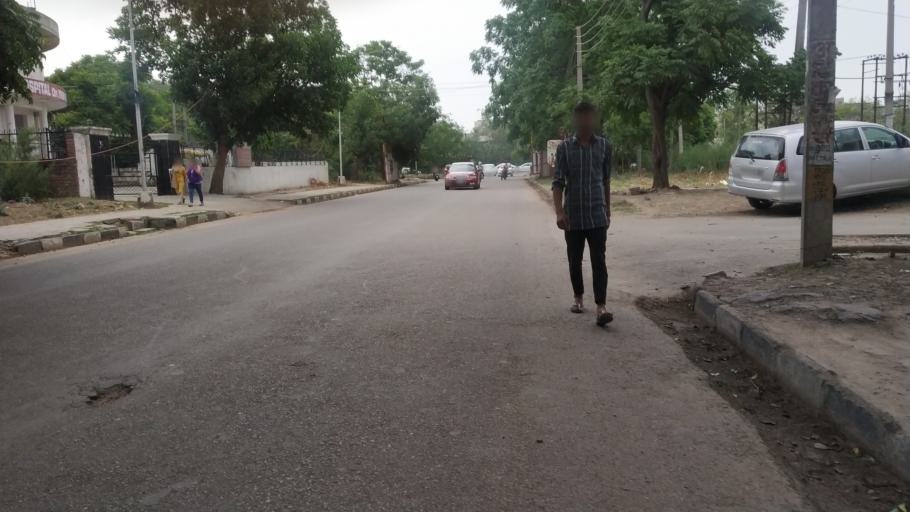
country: IN
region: Punjab
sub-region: Ajitgarh
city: Mohali
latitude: 30.6953
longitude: 76.7165
